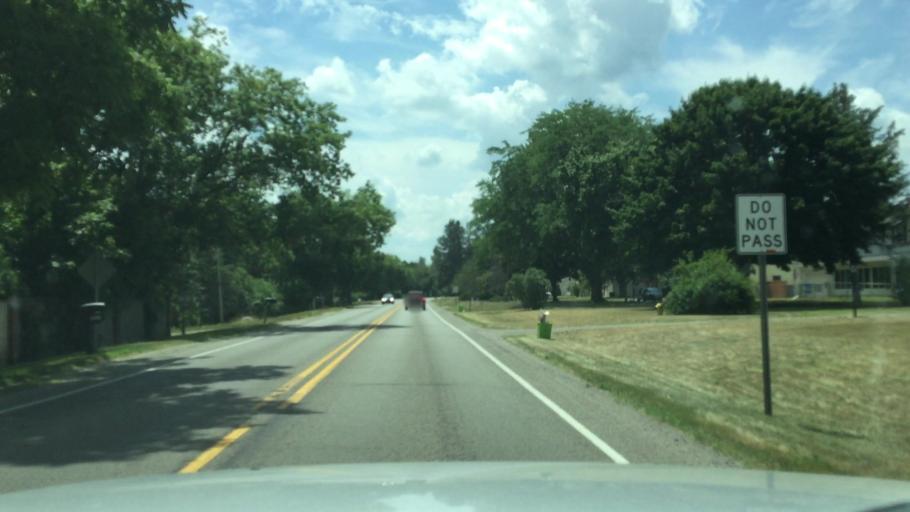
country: US
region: Michigan
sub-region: Genesee County
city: Flushing
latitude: 43.0876
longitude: -83.8664
